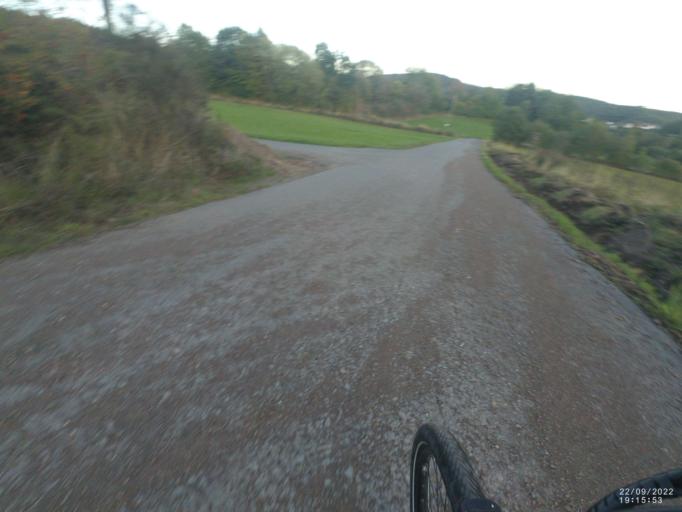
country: DE
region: Rheinland-Pfalz
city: Oberstadtfeld
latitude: 50.1818
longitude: 6.7594
